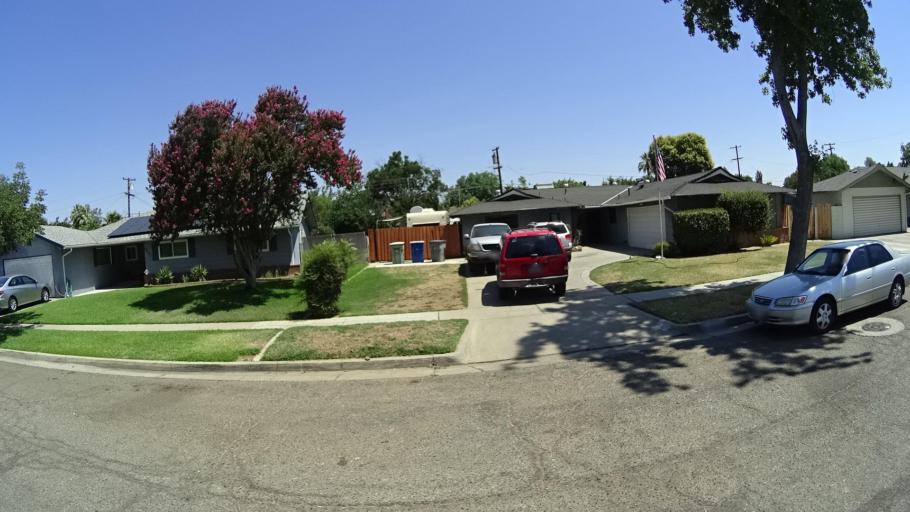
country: US
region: California
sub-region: Fresno County
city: Fresno
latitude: 36.8030
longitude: -119.7631
